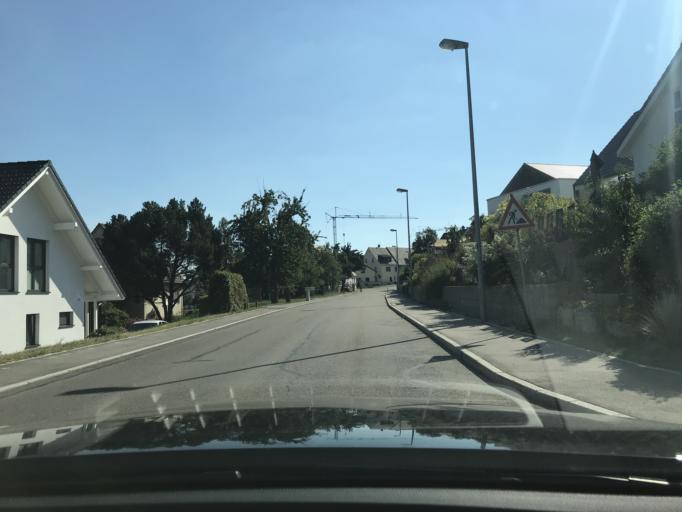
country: DE
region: Baden-Wuerttemberg
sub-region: Regierungsbezirk Stuttgart
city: Baltmannsweiler
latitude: 48.7536
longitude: 9.4855
